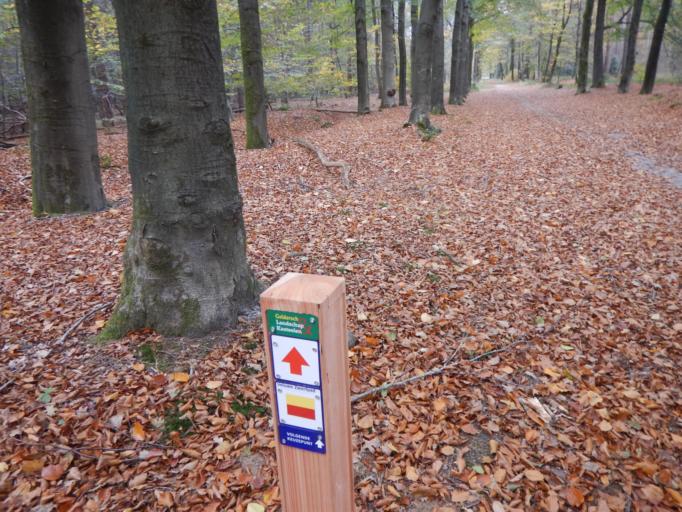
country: NL
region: Gelderland
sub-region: Gemeente Apeldoorn
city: Uddel
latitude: 52.2778
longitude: 5.7505
